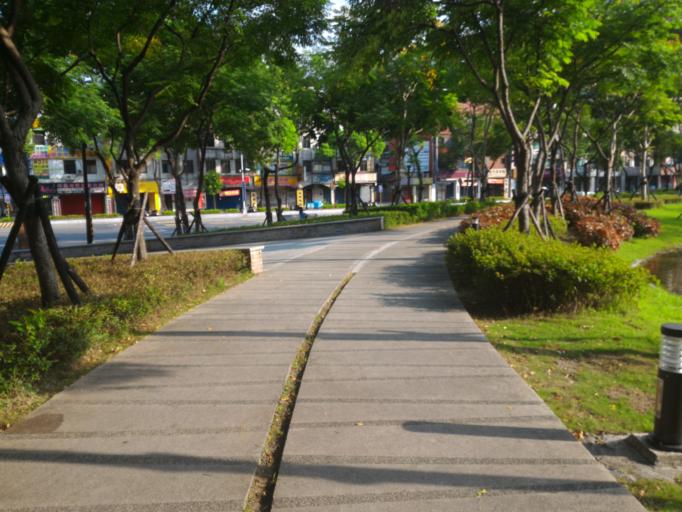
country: TW
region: Taipei
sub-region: Taipei
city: Banqiao
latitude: 25.0126
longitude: 121.4608
